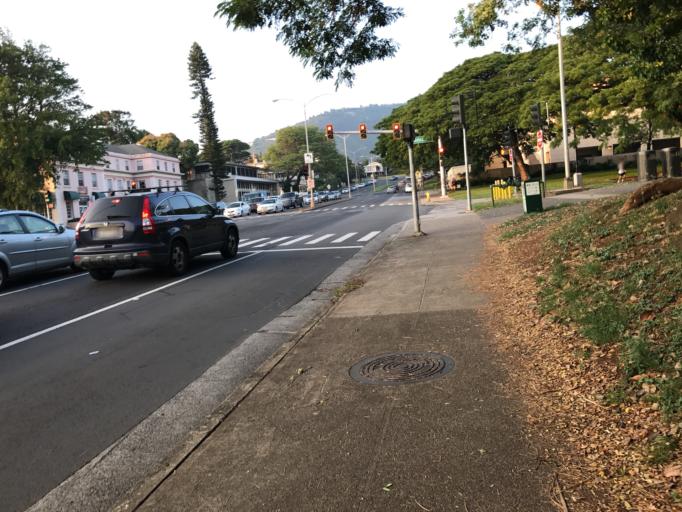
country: US
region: Hawaii
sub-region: Honolulu County
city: Honolulu
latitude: 21.2988
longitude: -157.8210
